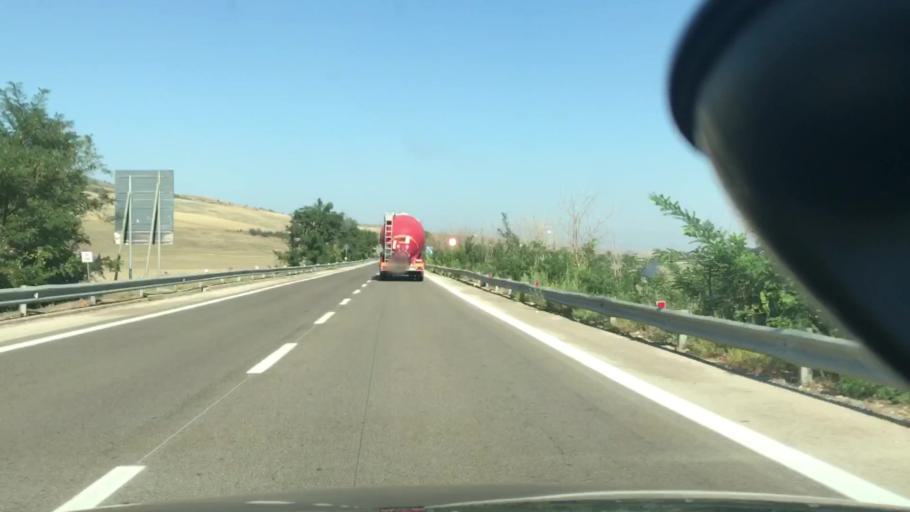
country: IT
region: Basilicate
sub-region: Provincia di Matera
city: Irsina
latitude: 40.7924
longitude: 16.2809
